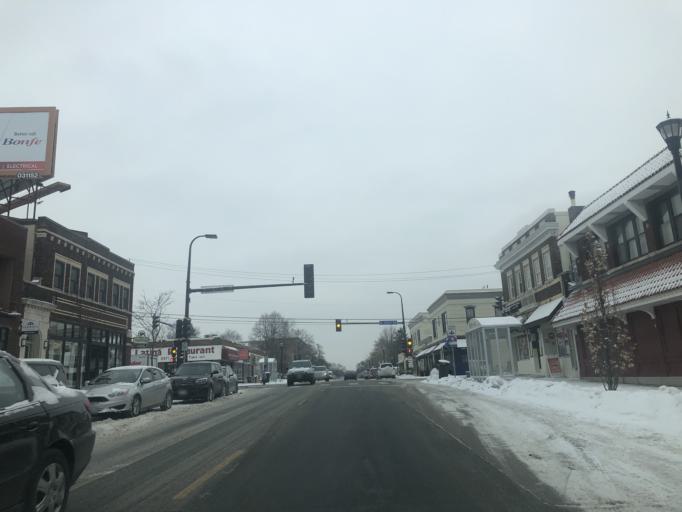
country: US
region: Minnesota
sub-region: Hennepin County
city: Minneapolis
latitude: 44.9337
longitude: -93.2779
